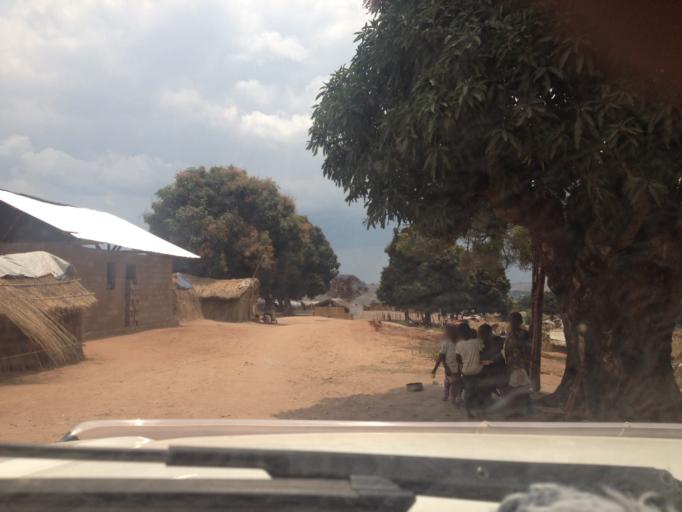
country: CD
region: Katanga
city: Kalemie
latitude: -5.9284
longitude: 29.1740
